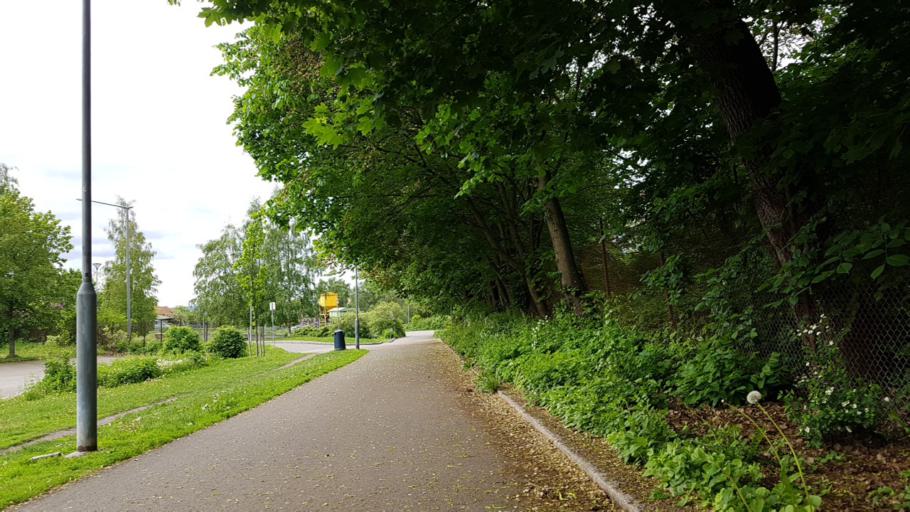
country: NO
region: Oslo
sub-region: Oslo
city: Oslo
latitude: 59.9319
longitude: 10.7726
